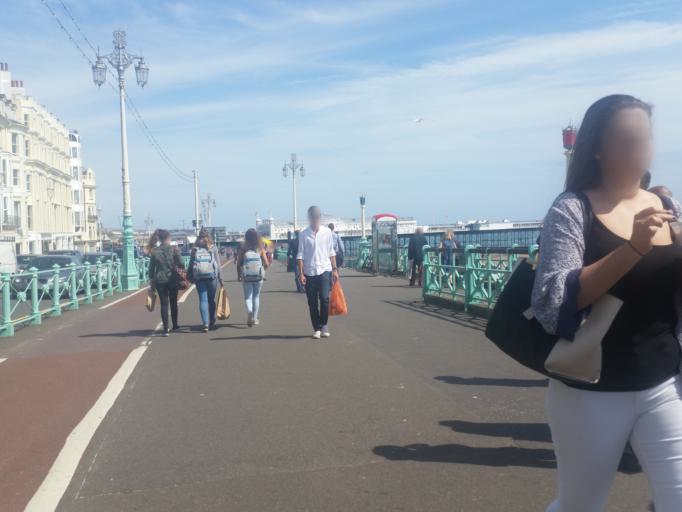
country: GB
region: England
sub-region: Brighton and Hove
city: Brighton
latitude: 50.8198
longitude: -0.1408
